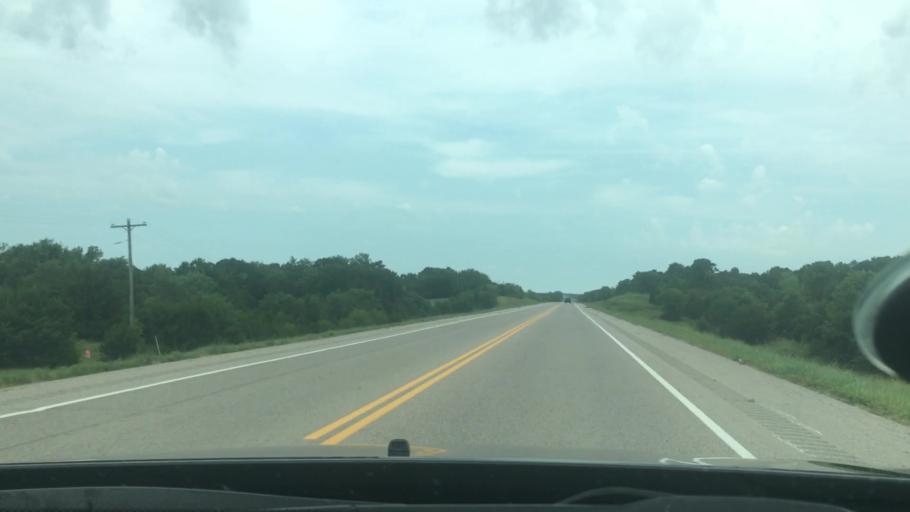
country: US
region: Oklahoma
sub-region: Seminole County
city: Konawa
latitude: 34.9957
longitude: -96.6790
